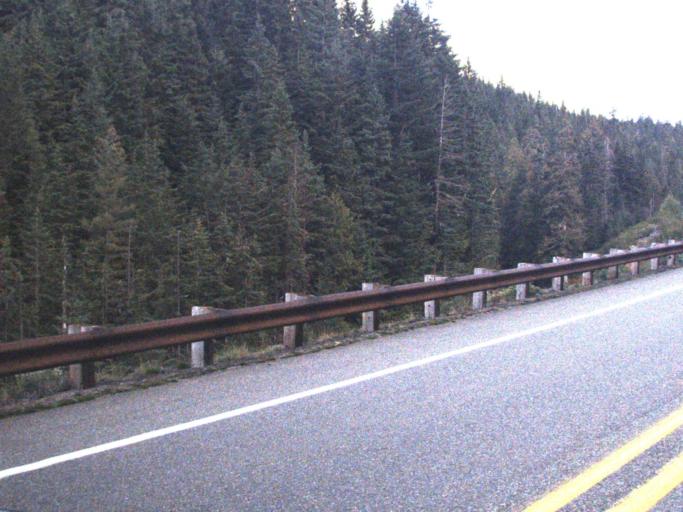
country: US
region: Washington
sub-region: Snohomish County
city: Darrington
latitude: 48.6304
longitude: -120.8454
